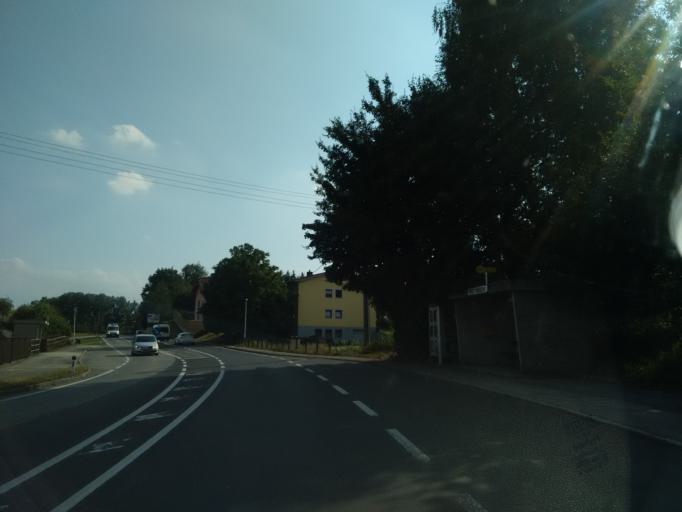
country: AT
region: Upper Austria
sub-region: Politischer Bezirk Grieskirchen
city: Bad Schallerbach
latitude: 48.2251
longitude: 13.9639
